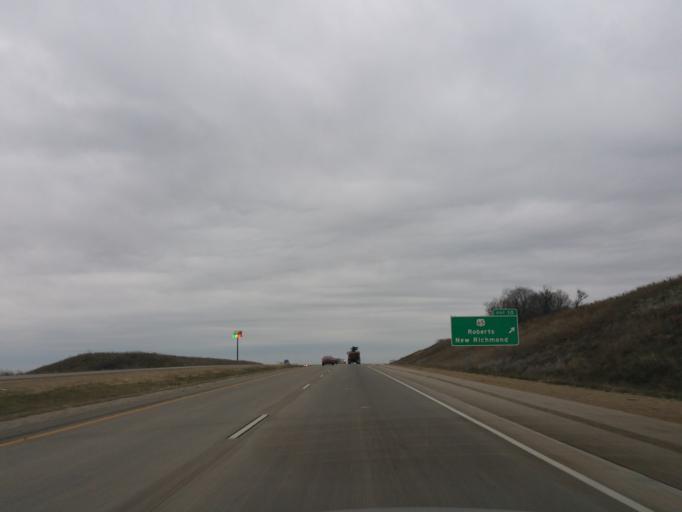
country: US
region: Wisconsin
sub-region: Saint Croix County
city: Roberts
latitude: 44.9603
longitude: -92.5711
